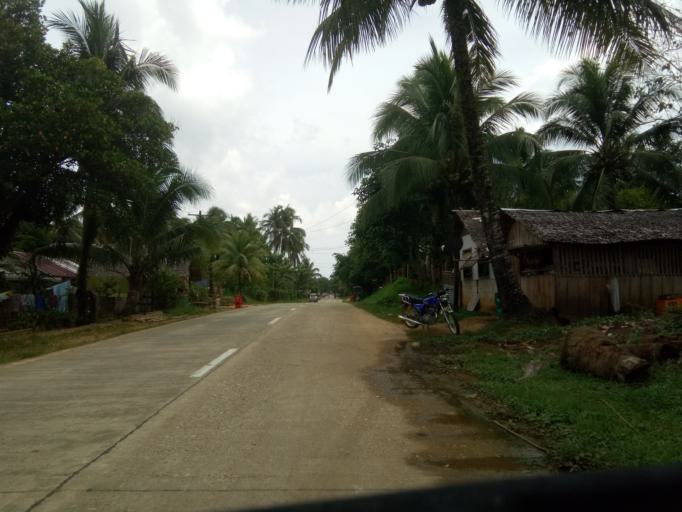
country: PH
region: Caraga
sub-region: Province of Surigao del Norte
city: San Isidro
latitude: 9.9289
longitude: 126.0589
